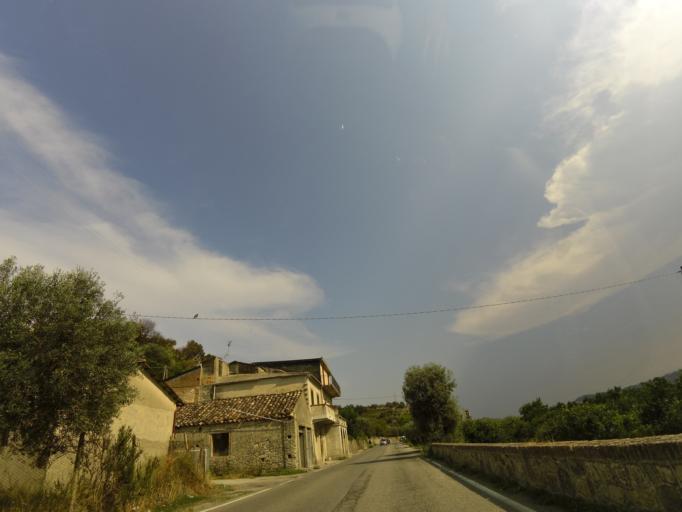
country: IT
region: Calabria
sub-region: Provincia di Reggio Calabria
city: Monasterace
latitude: 38.4572
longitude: 16.5254
